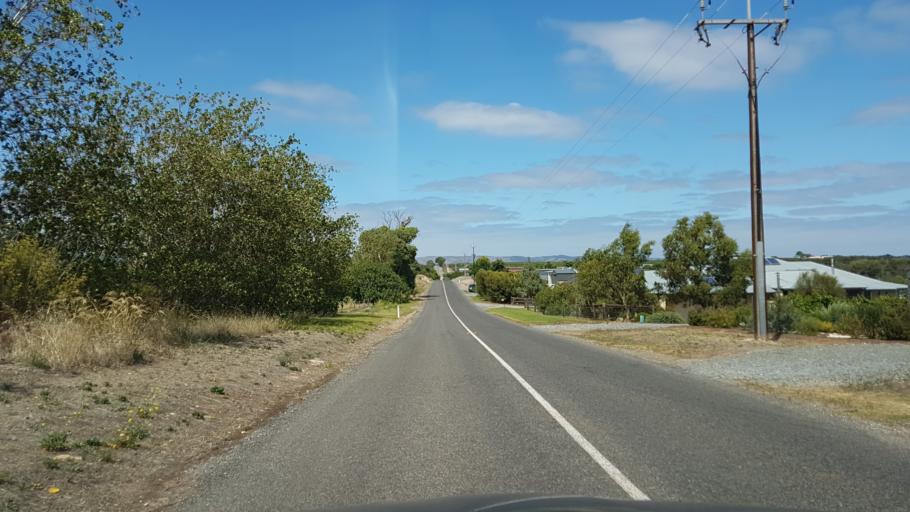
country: AU
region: South Australia
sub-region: Onkaparinga
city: McLaren Vale
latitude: -35.2156
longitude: 138.5177
